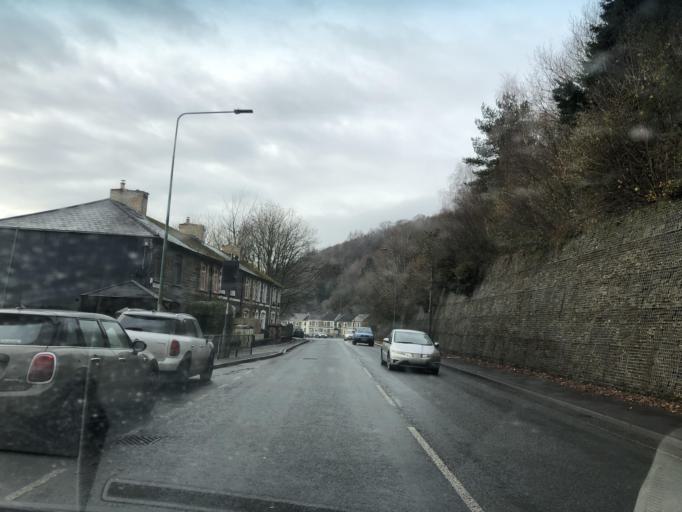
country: GB
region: Wales
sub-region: Blaenau Gwent
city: Abertillery
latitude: 51.7184
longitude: -3.1358
